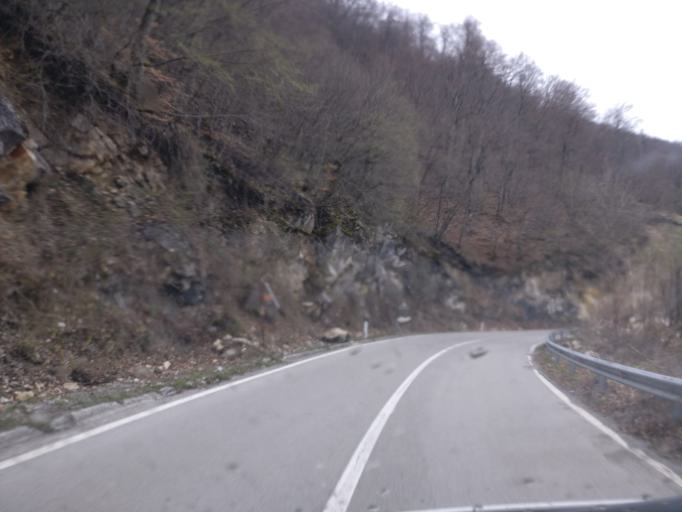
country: ME
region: Opstina Pluzine
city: Pluzine
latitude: 43.1413
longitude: 18.8312
